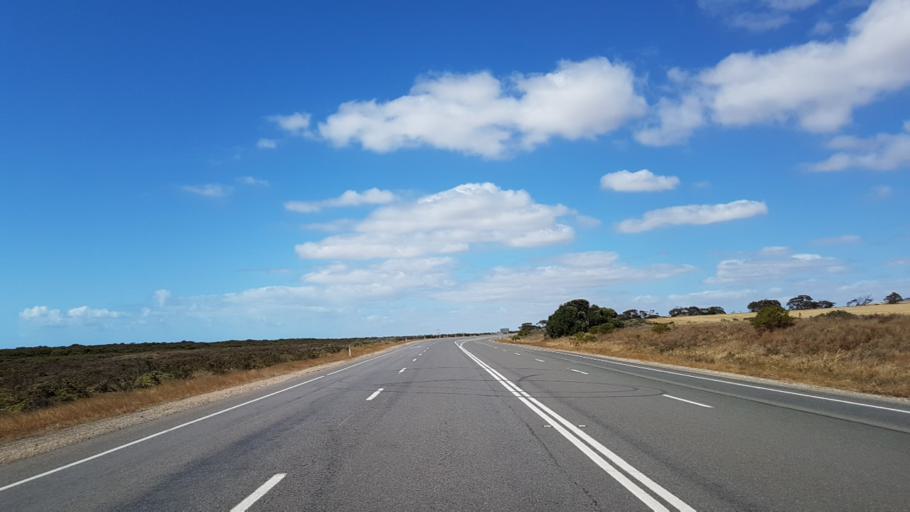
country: AU
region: South Australia
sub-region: Yorke Peninsula
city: Ardrossan
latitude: -34.1775
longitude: 138.0408
